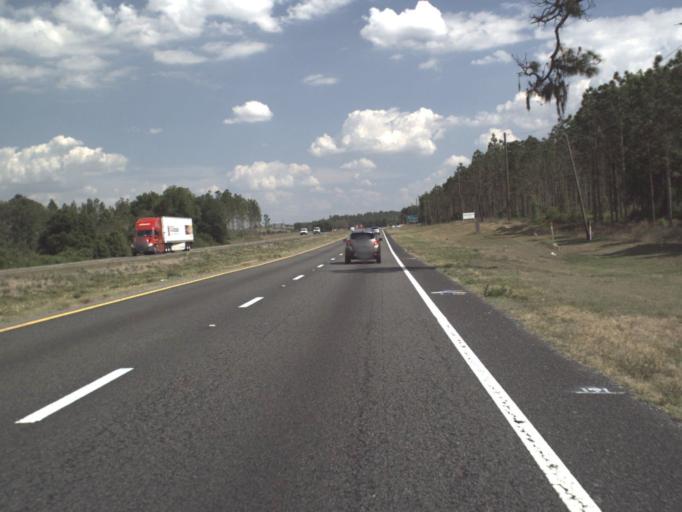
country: US
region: Florida
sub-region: Lake County
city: Mascotte
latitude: 28.6548
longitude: -81.8428
